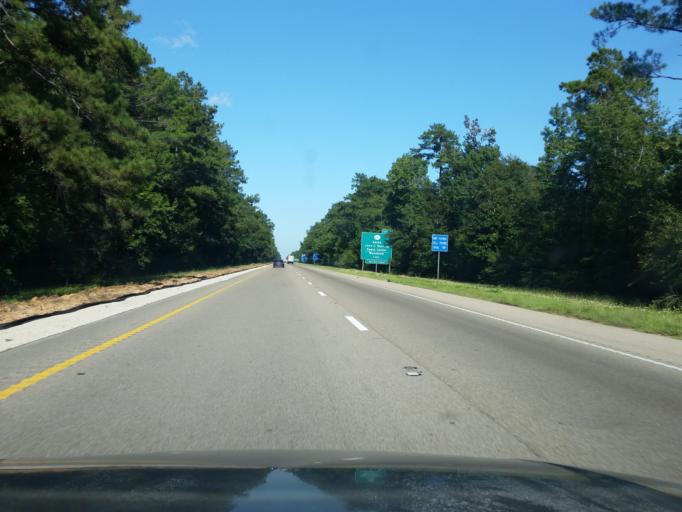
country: US
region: Mississippi
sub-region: Hancock County
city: Pearlington
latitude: 30.3090
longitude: -89.6192
